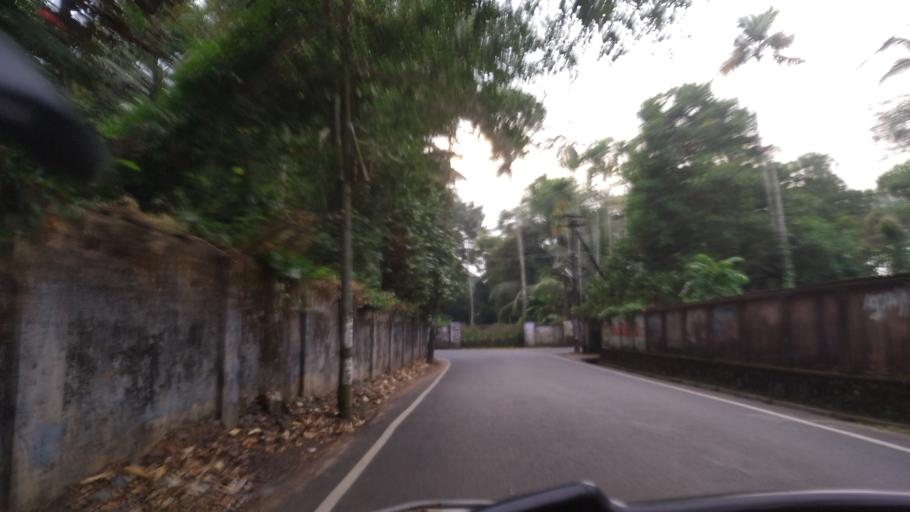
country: IN
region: Kerala
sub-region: Thrissur District
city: Kodungallur
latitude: 10.1378
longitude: 76.2257
